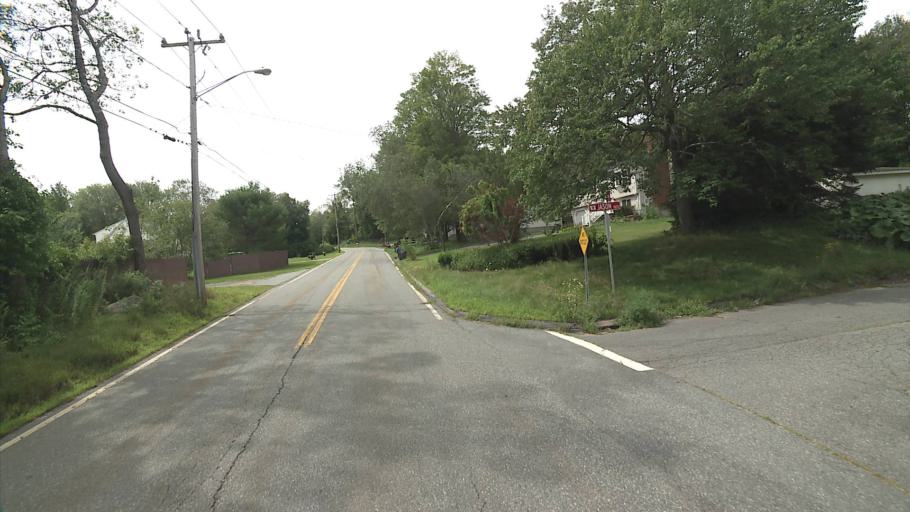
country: US
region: Connecticut
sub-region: Windham County
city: Thompson
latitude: 41.9877
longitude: -71.8438
